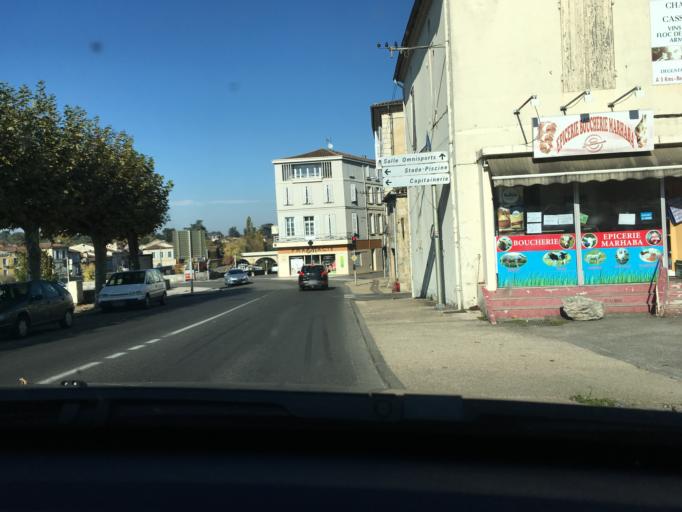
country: FR
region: Midi-Pyrenees
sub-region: Departement du Gers
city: Condom
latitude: 43.9562
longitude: 0.3692
